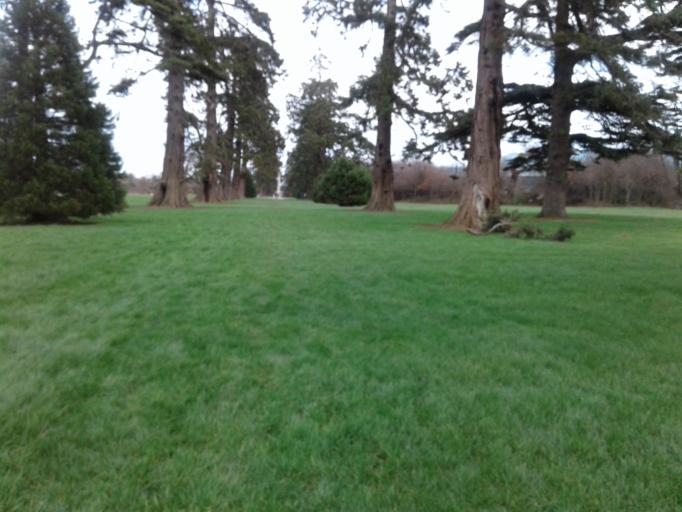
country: IE
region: Leinster
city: Beaumont
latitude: 53.4011
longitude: -6.2482
